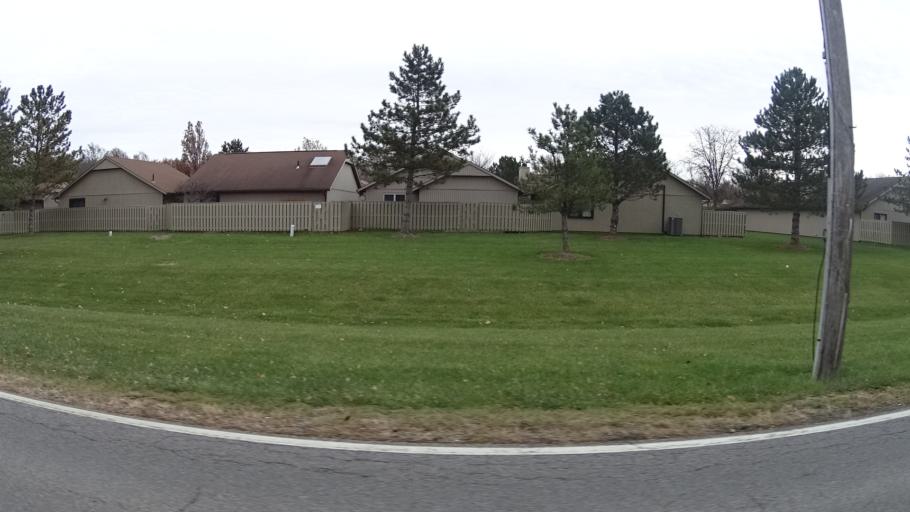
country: US
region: Ohio
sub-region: Cuyahoga County
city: Berea
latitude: 41.3366
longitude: -81.8772
